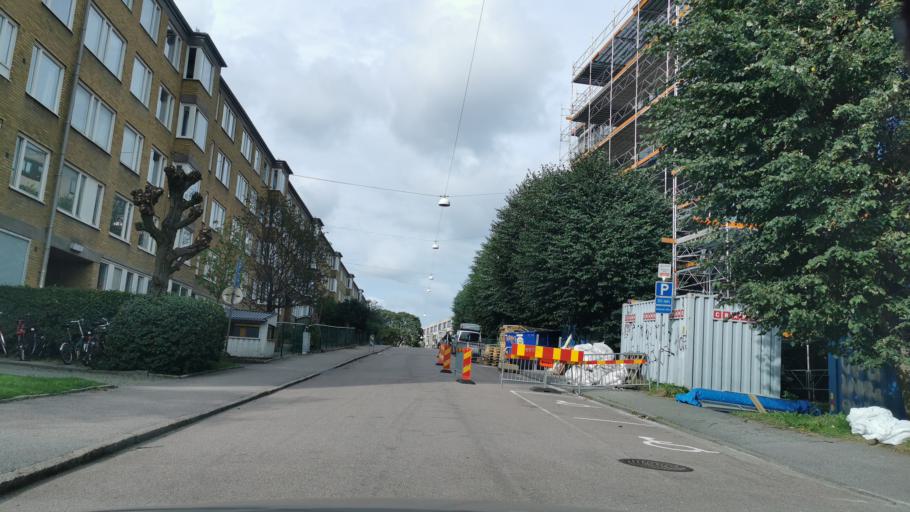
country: SE
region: Vaestra Goetaland
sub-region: Goteborg
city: Goeteborg
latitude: 57.6909
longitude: 11.9466
